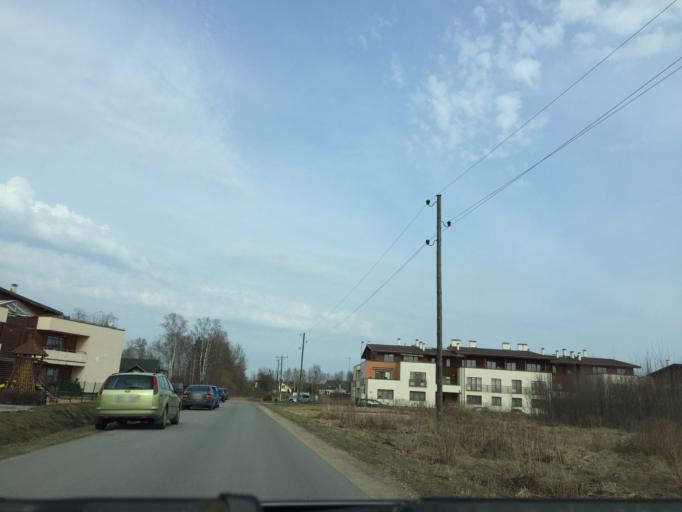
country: LV
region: Kekava
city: Balozi
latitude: 56.8744
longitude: 24.1498
